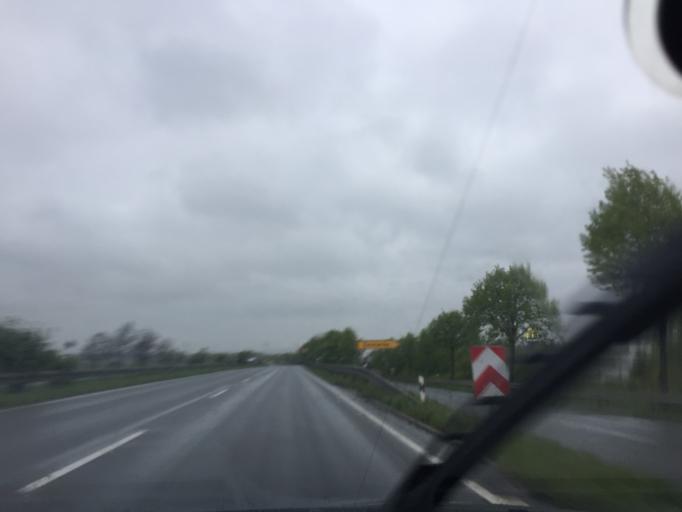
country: DE
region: Lower Saxony
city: Giesen
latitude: 52.1590
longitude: 9.8696
